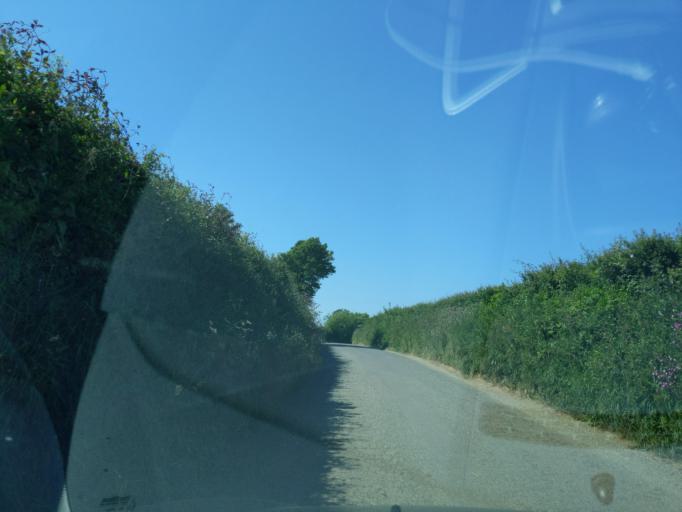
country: GB
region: England
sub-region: Cornwall
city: Wadebridge
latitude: 50.5774
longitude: -4.8307
